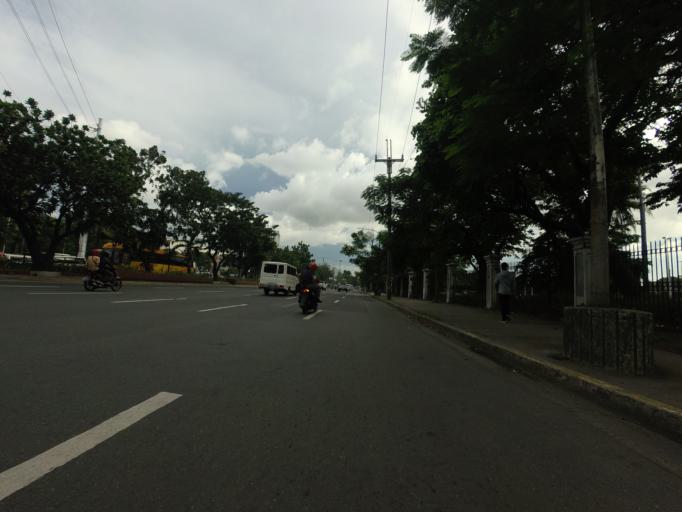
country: PH
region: Metro Manila
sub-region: City of Manila
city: Quiapo
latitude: 14.5917
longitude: 120.9802
